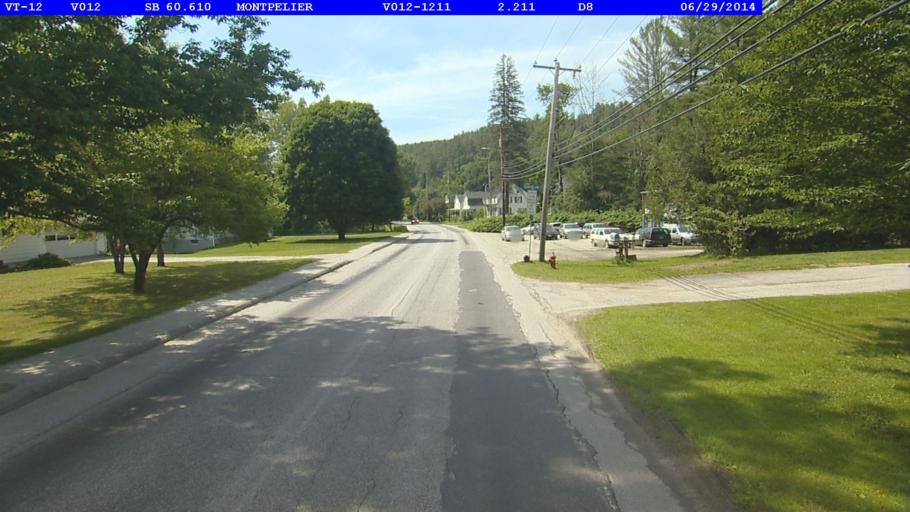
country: US
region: Vermont
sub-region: Washington County
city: Montpelier
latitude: 44.2750
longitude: -72.5732
